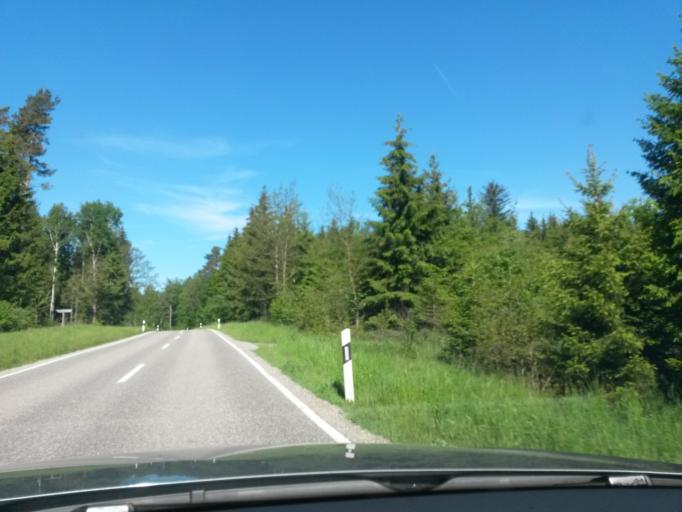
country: DE
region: Baden-Wuerttemberg
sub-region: Tuebingen Region
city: Kanzach
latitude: 48.0776
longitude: 9.5199
